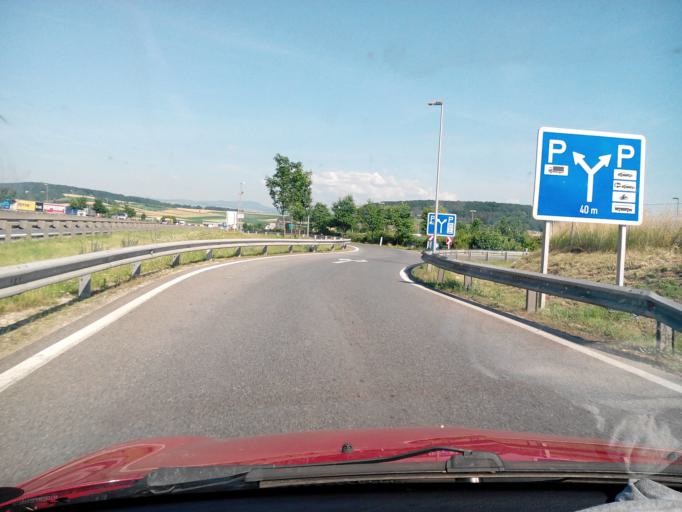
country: AT
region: Lower Austria
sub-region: Politischer Bezirk Melk
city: Loosdorf
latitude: 48.1937
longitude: 15.3847
